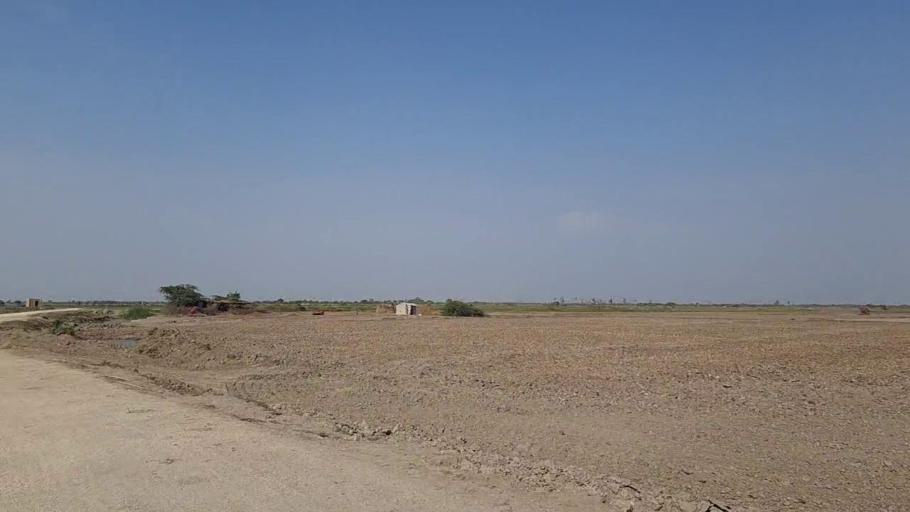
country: PK
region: Sindh
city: Daro Mehar
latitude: 24.7597
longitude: 68.1662
